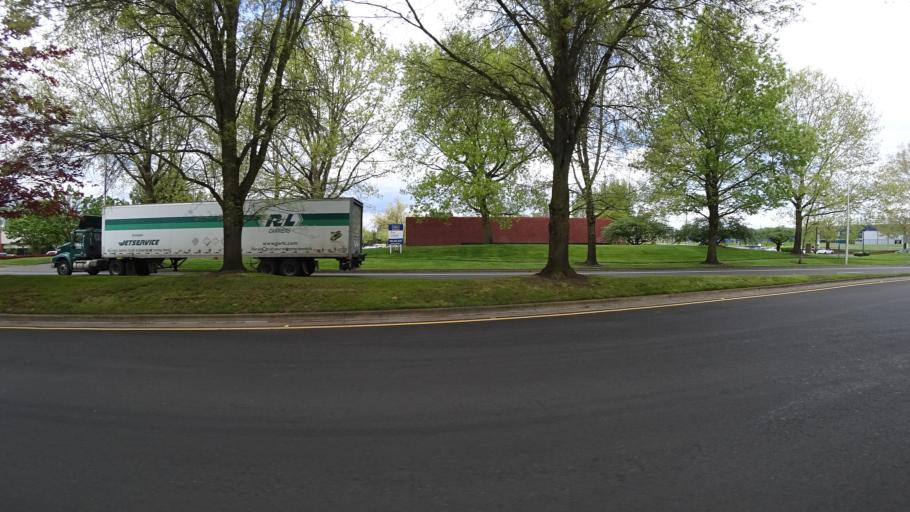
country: US
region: Oregon
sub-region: Washington County
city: Rockcreek
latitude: 45.5463
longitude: -122.9017
